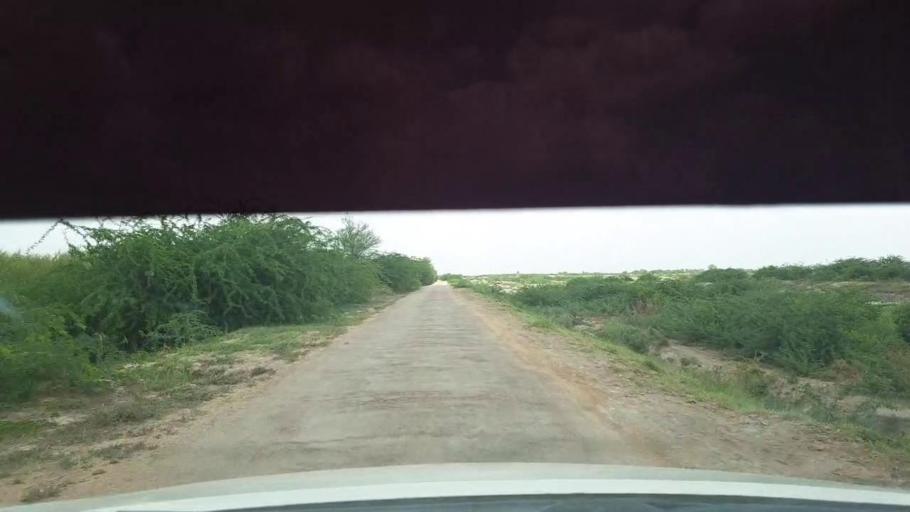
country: PK
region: Sindh
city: Kadhan
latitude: 24.4811
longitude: 69.0662
